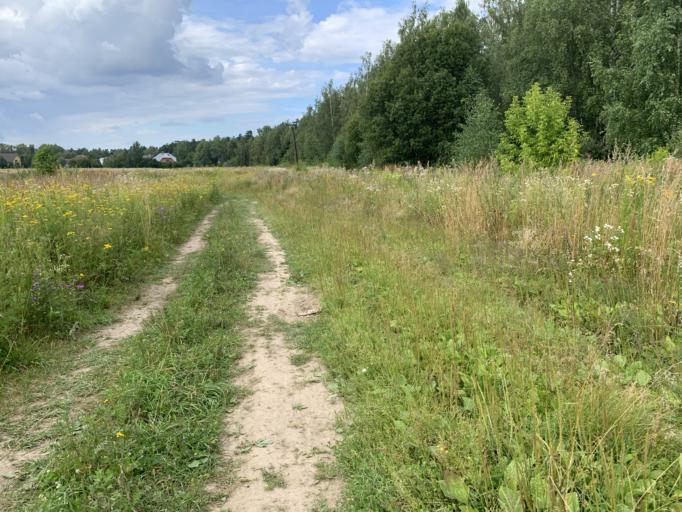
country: RU
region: Moskovskaya
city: Cherkizovo
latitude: 55.9935
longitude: 37.7990
